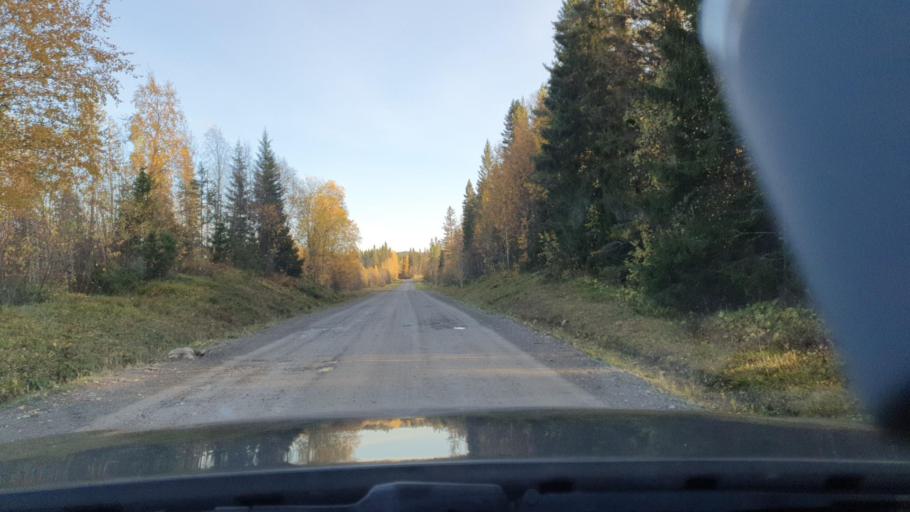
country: SE
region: Jaemtland
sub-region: Stroemsunds Kommun
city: Stroemsund
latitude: 63.5222
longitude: 15.6347
